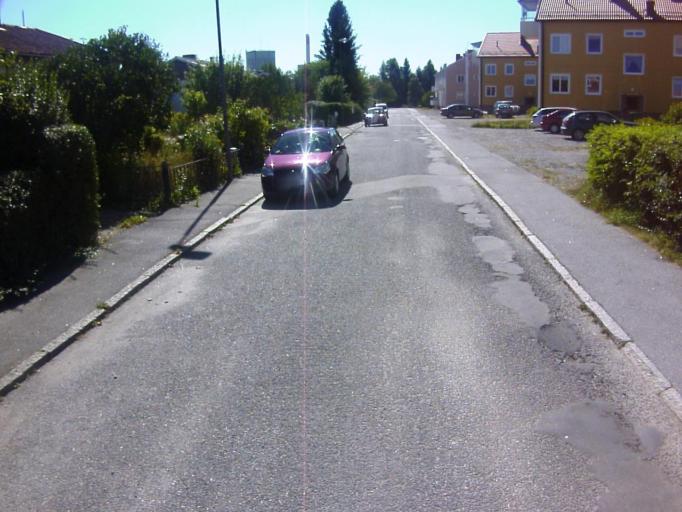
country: SE
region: Soedermanland
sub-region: Eskilstuna Kommun
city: Eskilstuna
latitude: 59.3861
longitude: 16.4975
